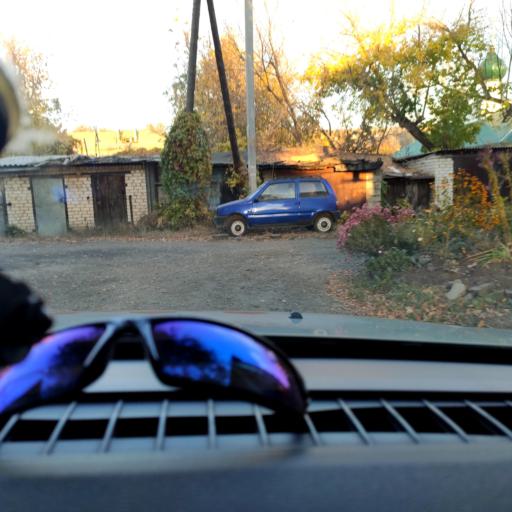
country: RU
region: Samara
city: Samara
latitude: 53.1732
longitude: 50.1731
